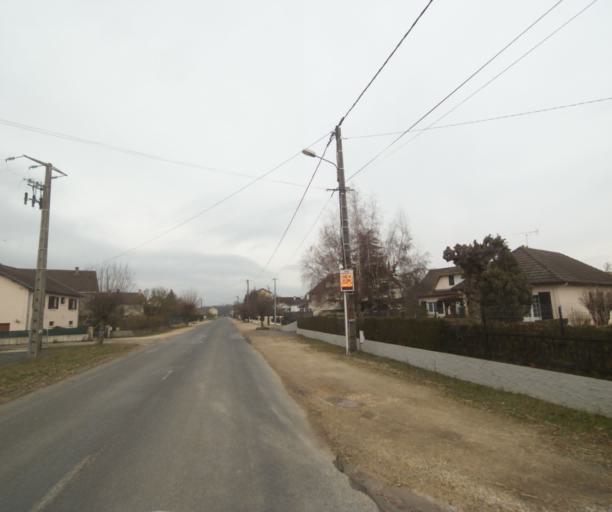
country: FR
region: Champagne-Ardenne
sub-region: Departement de la Haute-Marne
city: Villiers-en-Lieu
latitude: 48.6797
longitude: 4.8853
